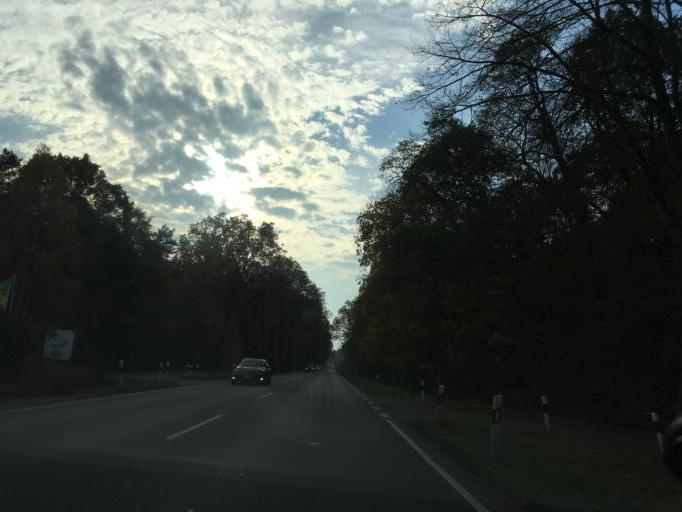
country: DE
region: Lower Saxony
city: Embsen
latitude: 53.1776
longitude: 10.3158
